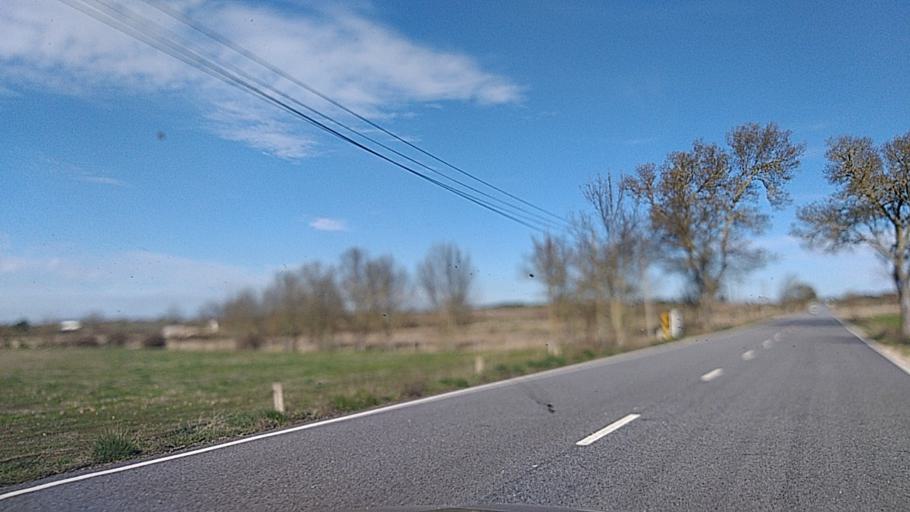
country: ES
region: Castille and Leon
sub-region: Provincia de Salamanca
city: Fuentes de Onoro
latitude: 40.5969
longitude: -6.9697
